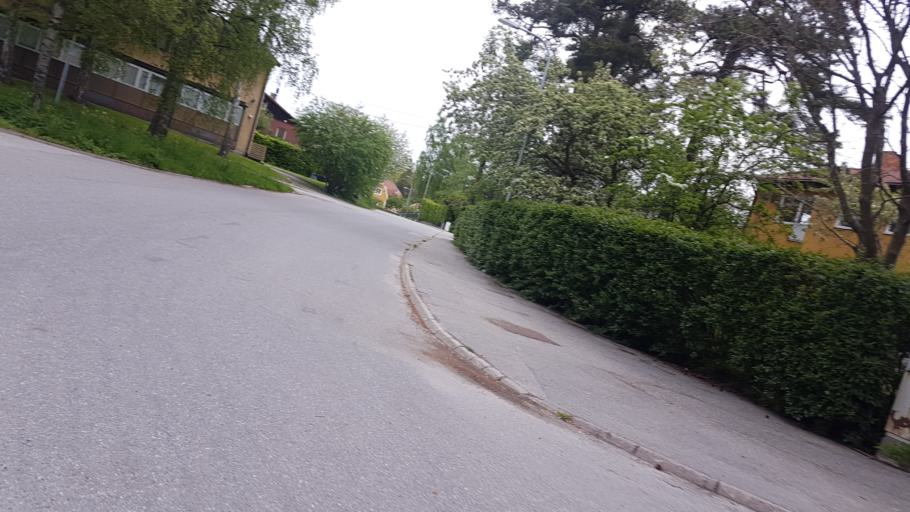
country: SE
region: Stockholm
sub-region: Lidingo
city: Lidingoe
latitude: 59.3560
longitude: 18.1441
